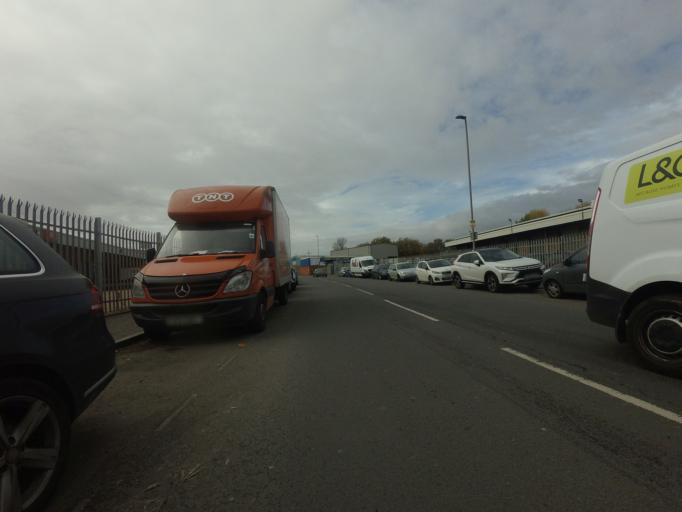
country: GB
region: England
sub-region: Greater London
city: Barking
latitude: 51.5253
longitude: 0.0973
